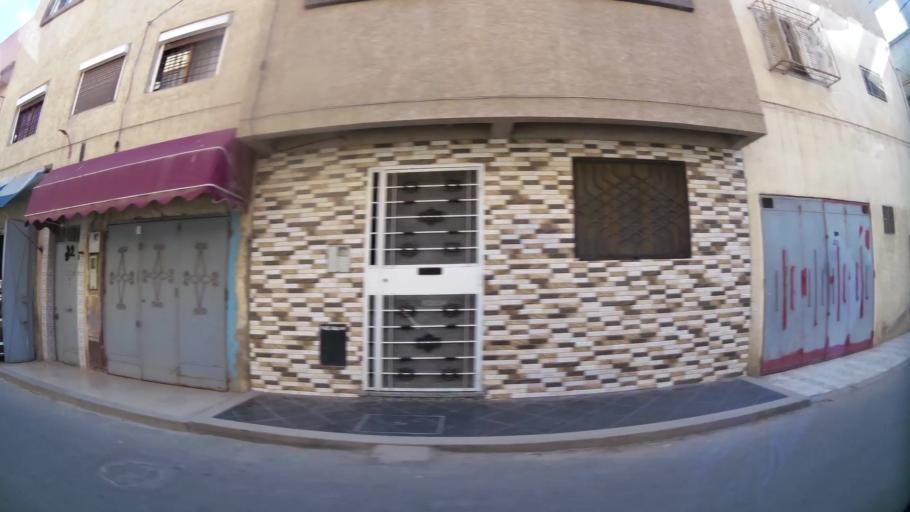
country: MA
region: Oriental
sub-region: Oujda-Angad
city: Oujda
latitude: 34.7115
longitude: -1.8852
